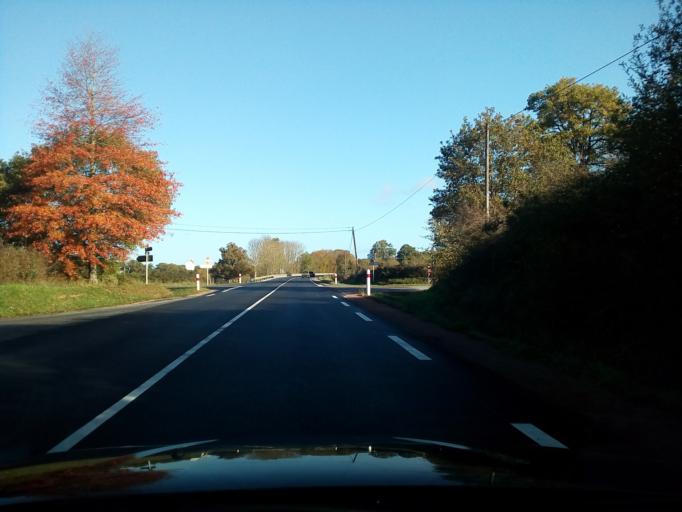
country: FR
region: Limousin
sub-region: Departement de la Haute-Vienne
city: Magnac-Laval
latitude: 46.1610
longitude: 1.1329
